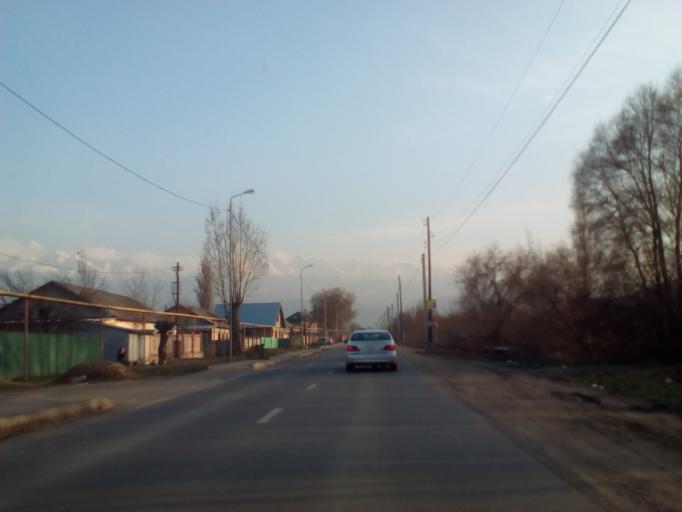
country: KZ
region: Almaty Oblysy
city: Burunday
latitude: 43.2453
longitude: 76.7465
